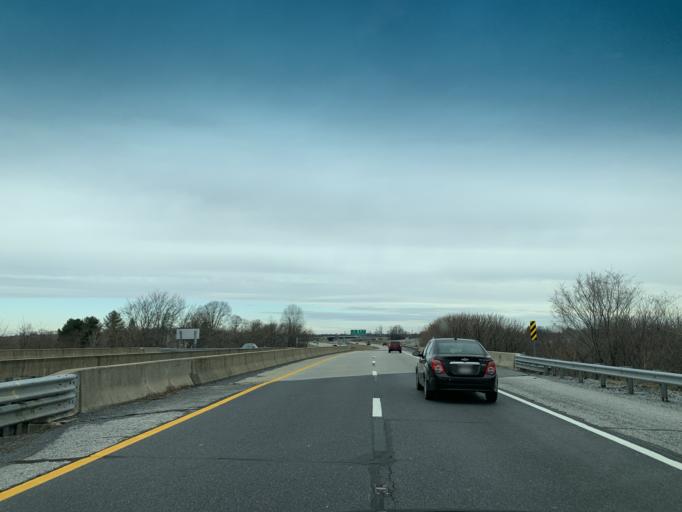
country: US
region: West Virginia
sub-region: Jefferson County
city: Ranson
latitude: 39.3261
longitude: -77.8535
